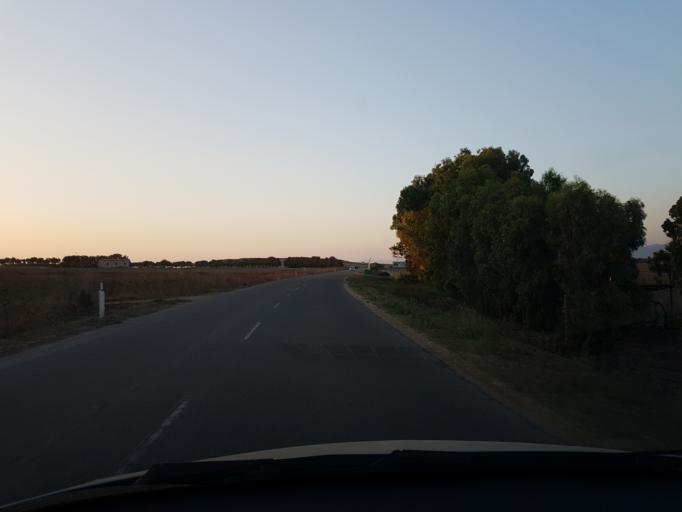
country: IT
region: Sardinia
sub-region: Provincia di Oristano
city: Nurachi
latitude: 39.9661
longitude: 8.4531
